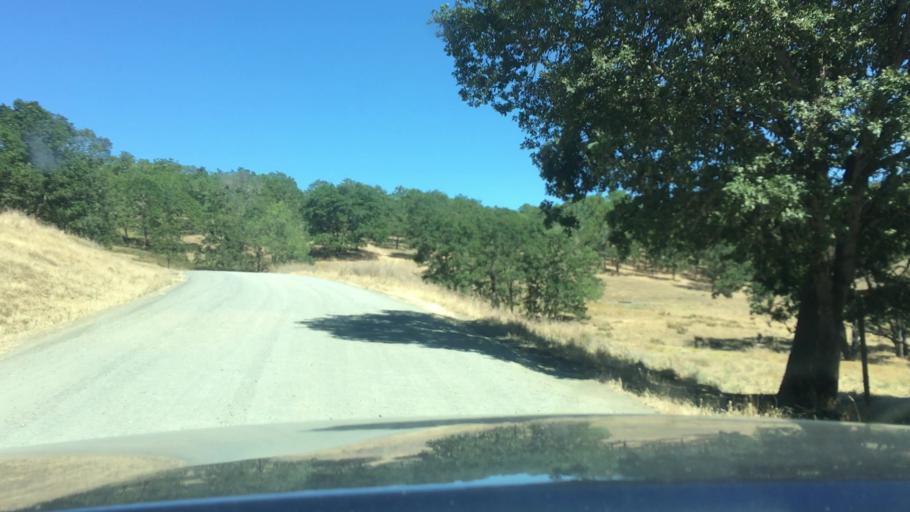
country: US
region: Oregon
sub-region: Douglas County
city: Winston
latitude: 43.1395
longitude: -123.4403
